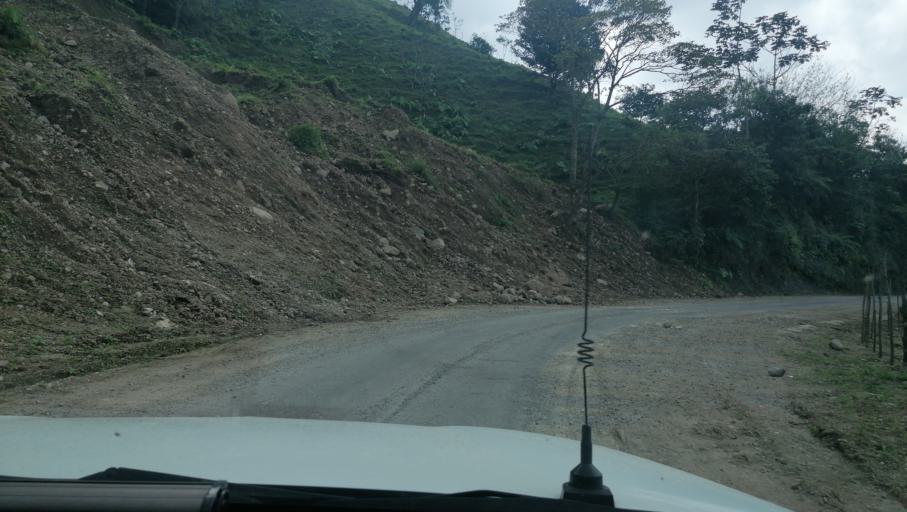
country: MX
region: Chiapas
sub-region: Francisco Leon
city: San Miguel la Sardina
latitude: 17.2385
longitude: -93.2999
